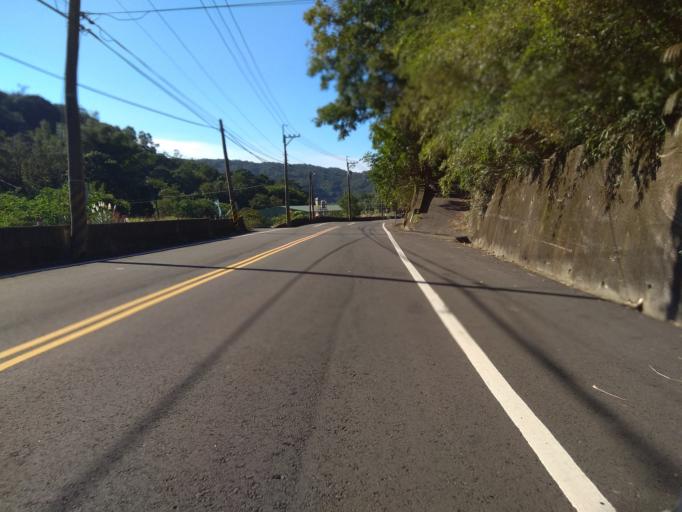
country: TW
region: Taiwan
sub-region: Hsinchu
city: Zhubei
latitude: 24.8529
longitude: 121.1467
